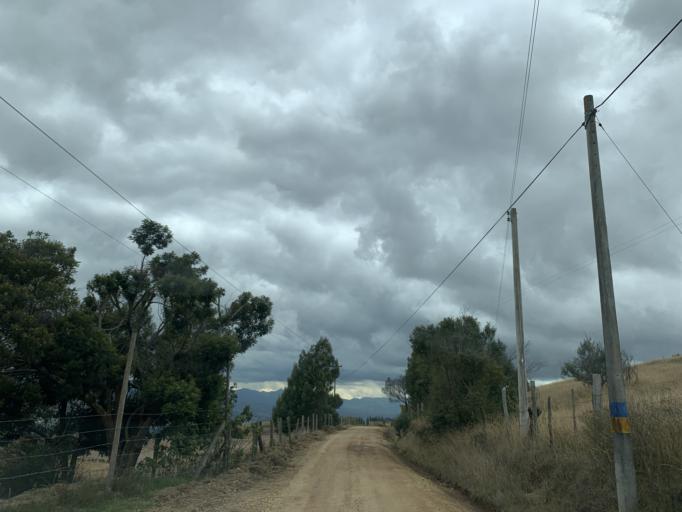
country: CO
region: Boyaca
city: Tunja
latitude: 5.5540
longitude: -73.3168
